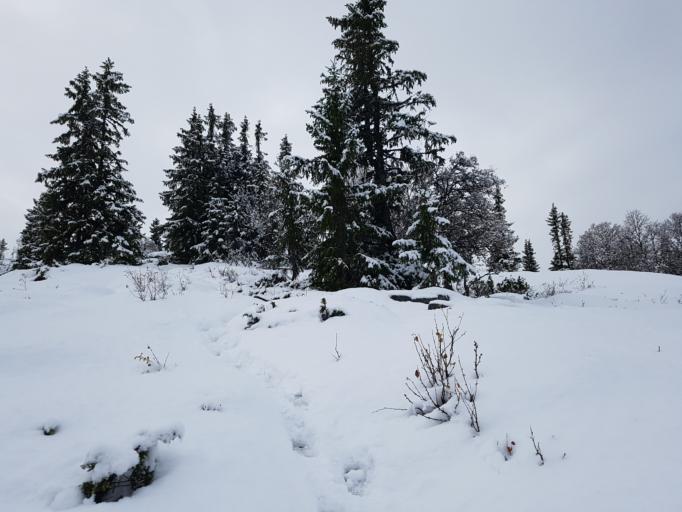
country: NO
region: Oppland
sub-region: Sel
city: Otta
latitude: 61.8053
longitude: 9.6772
